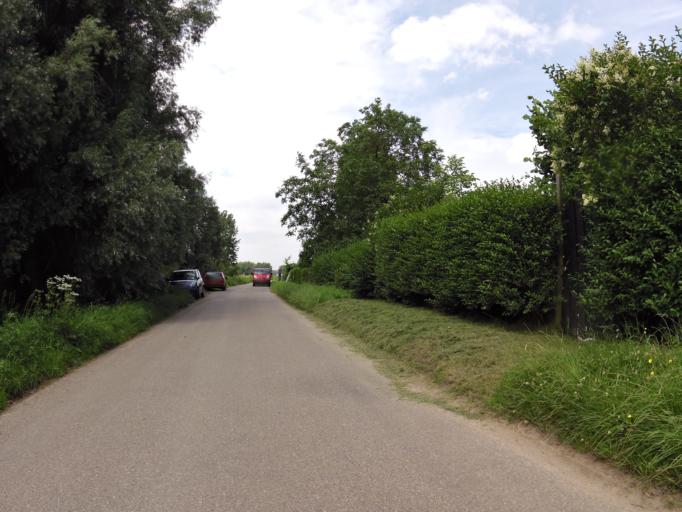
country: NL
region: South Holland
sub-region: Gemeente Leerdam
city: Leerdam
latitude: 51.8902
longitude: 5.1539
